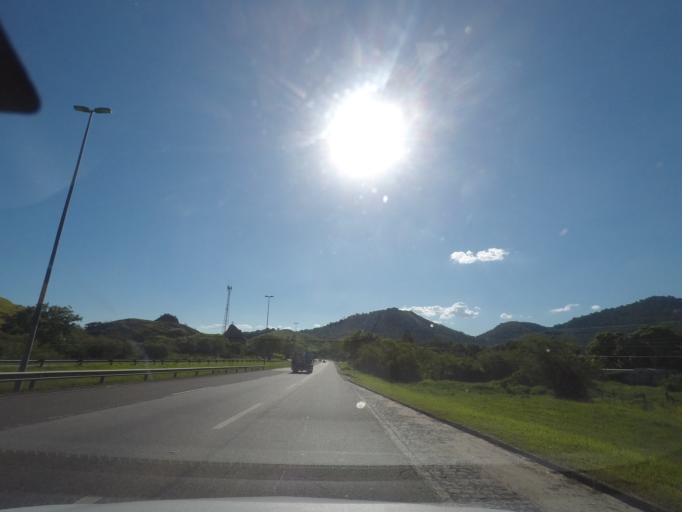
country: BR
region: Rio de Janeiro
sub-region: Guapimirim
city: Guapimirim
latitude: -22.6533
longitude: -43.0826
